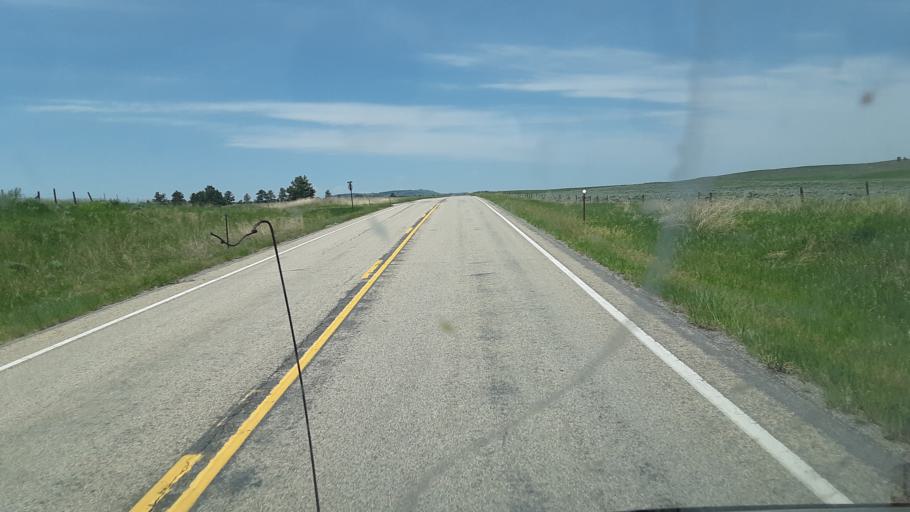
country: US
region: Montana
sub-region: Stillwater County
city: Columbus
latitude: 45.4809
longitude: -109.0136
